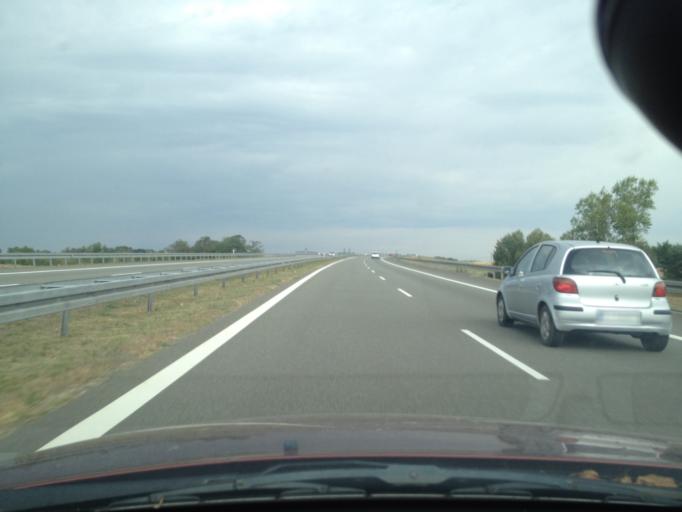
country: PL
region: Lubusz
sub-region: Powiat zielonogorski
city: Sulechow
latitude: 52.0782
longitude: 15.5913
